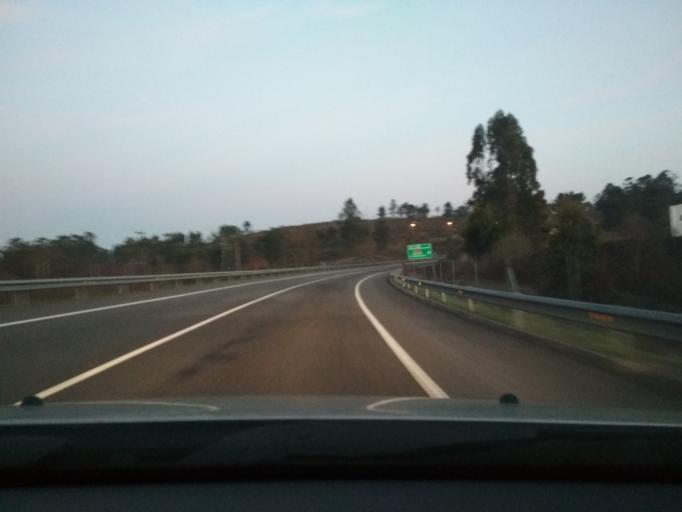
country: ES
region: Galicia
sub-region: Provincia da Coruna
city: Santiago de Compostela
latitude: 42.8365
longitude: -8.5914
